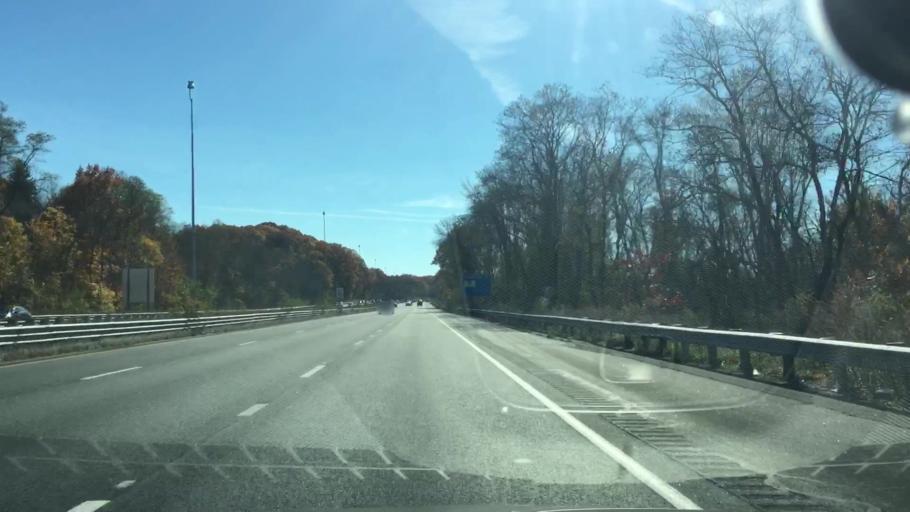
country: US
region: Massachusetts
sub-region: Hampden County
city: Longmeadow
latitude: 42.0444
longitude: -72.5891
